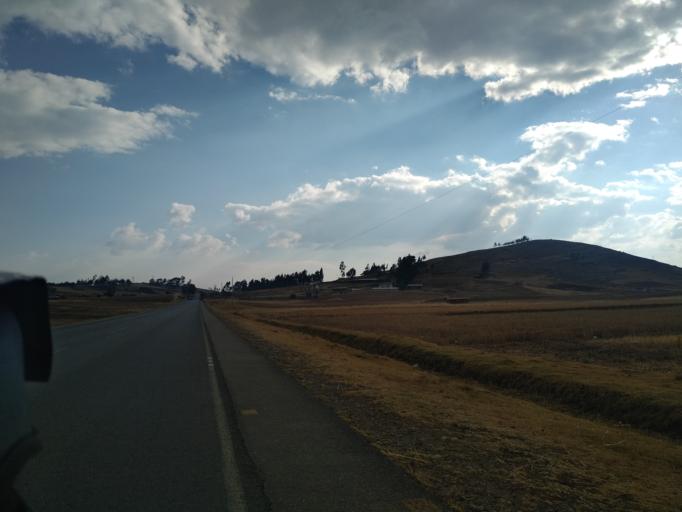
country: PE
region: Cajamarca
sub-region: Provincia de Cajamarca
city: Encanada
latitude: -7.1404
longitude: -78.3891
